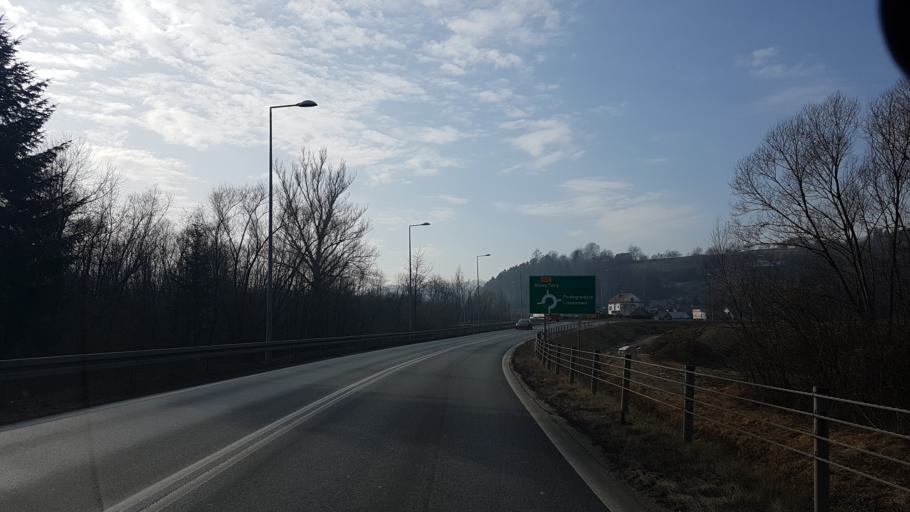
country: PL
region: Lesser Poland Voivodeship
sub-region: Powiat nowosadecki
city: Podegrodzie
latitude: 49.5584
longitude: 20.5778
